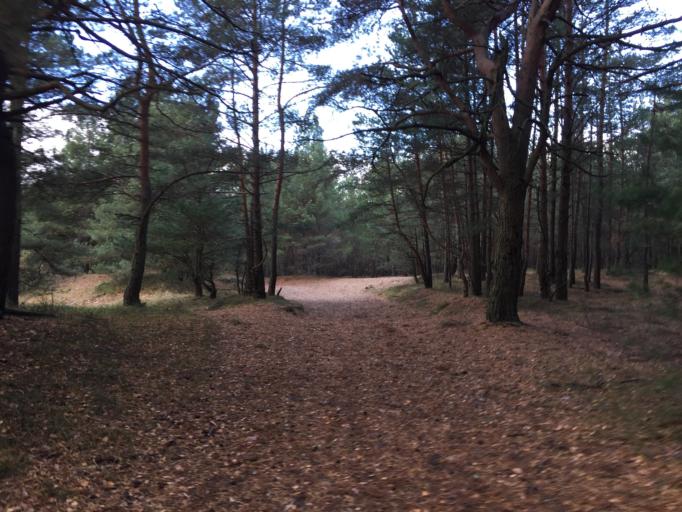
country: LV
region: Carnikava
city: Carnikava
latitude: 57.1543
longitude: 24.2776
